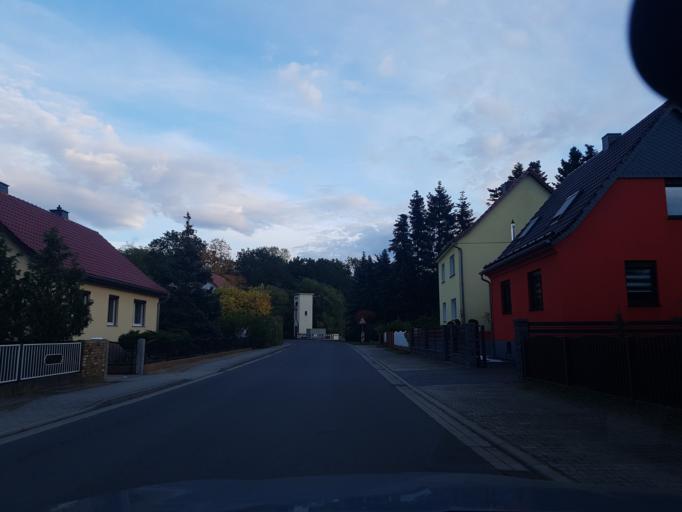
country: DE
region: Brandenburg
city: Elsterwerda
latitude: 51.4482
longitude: 13.5138
